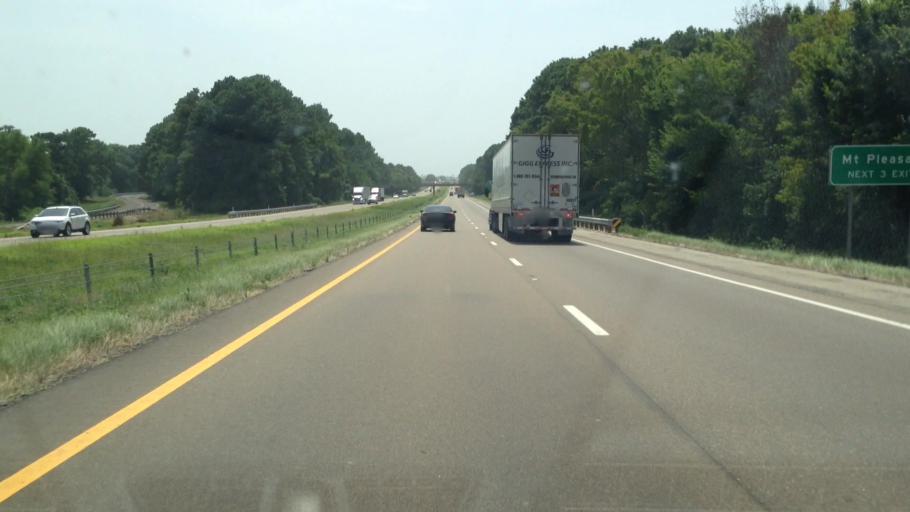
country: US
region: Texas
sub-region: Titus County
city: Mount Pleasant
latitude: 33.1902
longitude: -94.9394
